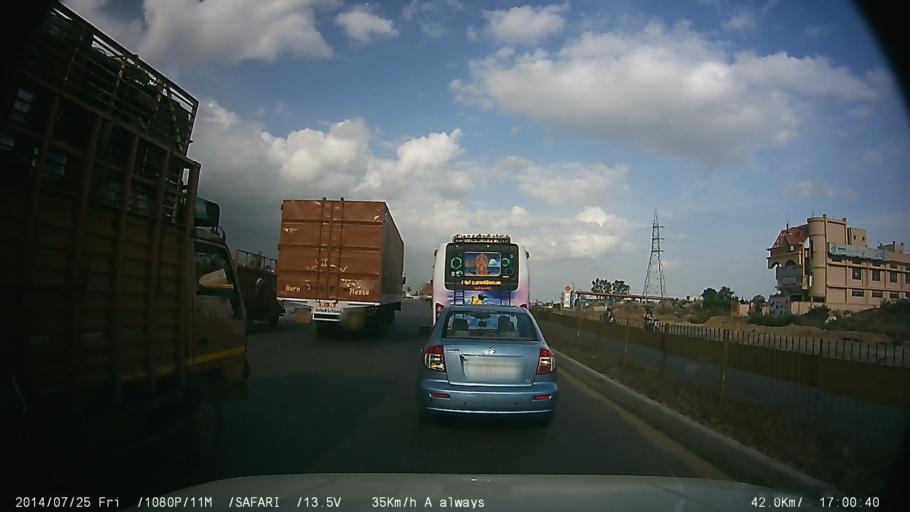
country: IN
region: Tamil Nadu
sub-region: Krishnagiri
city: Hosur
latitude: 12.7266
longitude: 77.8524
